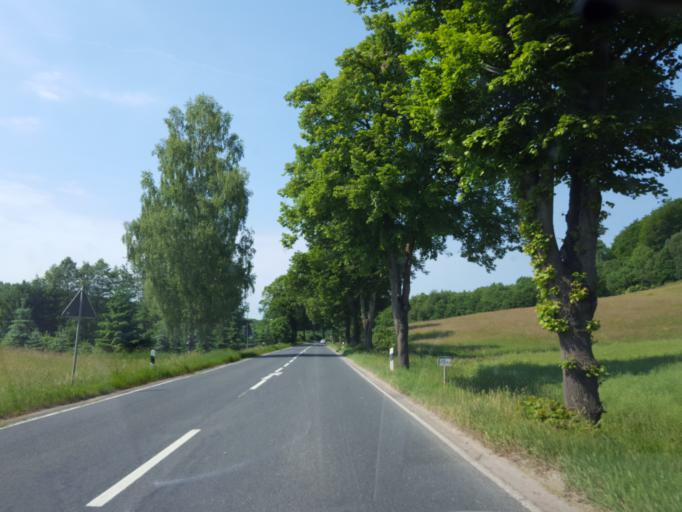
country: DE
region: Lower Saxony
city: Eisdorf am Harz
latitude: 51.7155
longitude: 10.1901
